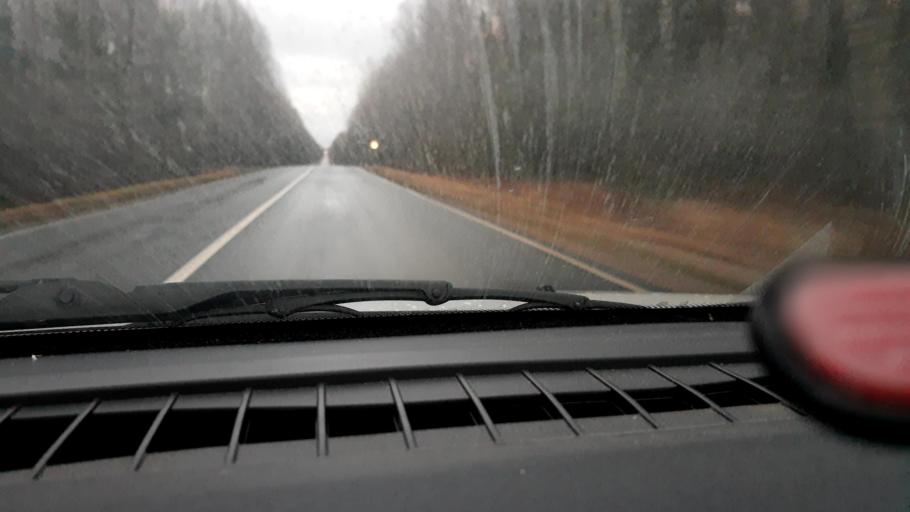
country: RU
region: Nizjnij Novgorod
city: Uren'
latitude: 57.2522
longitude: 45.6056
